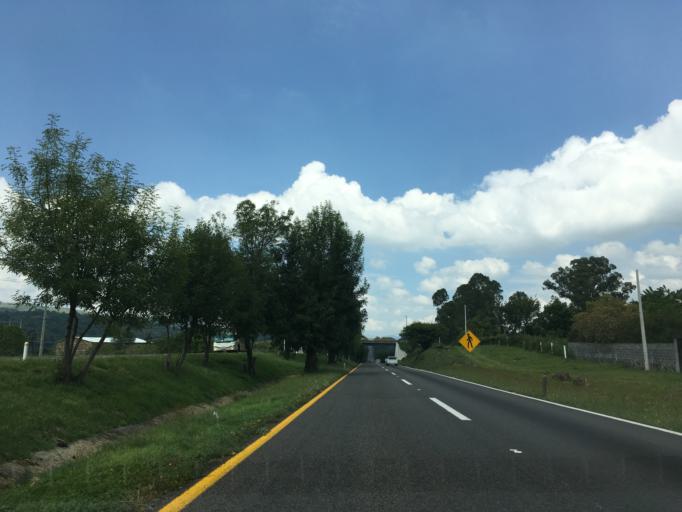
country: MX
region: Michoacan
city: Lagunillas
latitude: 19.5550
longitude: -101.3877
